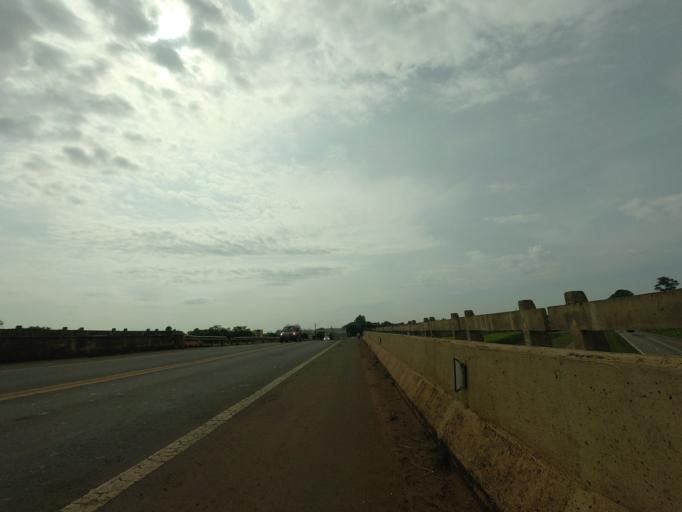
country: BR
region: Sao Paulo
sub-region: Piracicaba
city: Piracicaba
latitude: -22.7648
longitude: -47.5955
